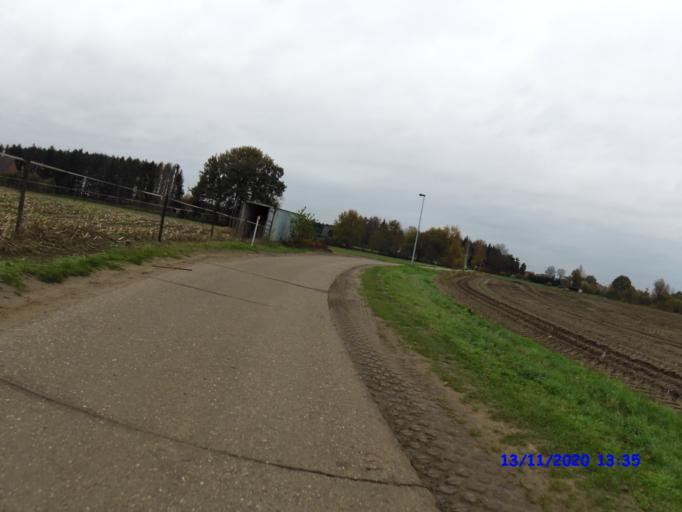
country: BE
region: Flanders
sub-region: Provincie Antwerpen
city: Kasterlee
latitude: 51.2419
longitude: 5.0023
